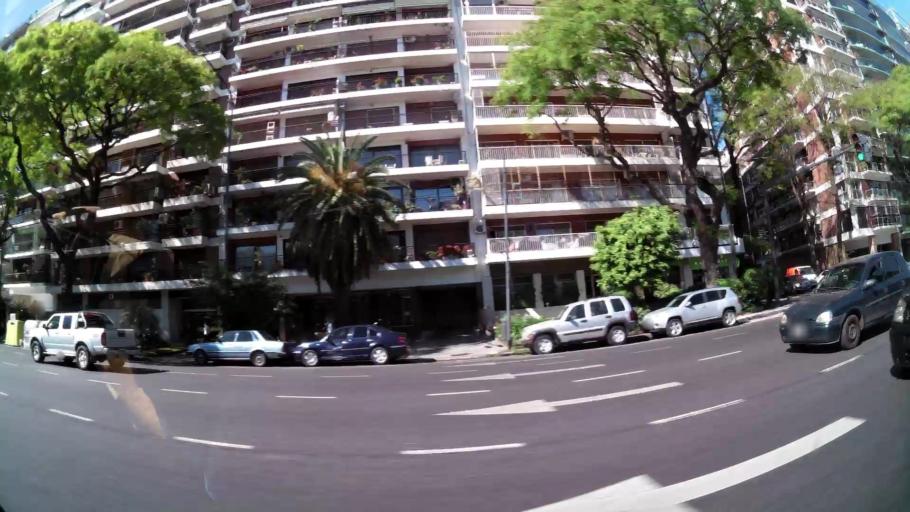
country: AR
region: Buenos Aires F.D.
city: Colegiales
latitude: -34.5631
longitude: -58.4379
